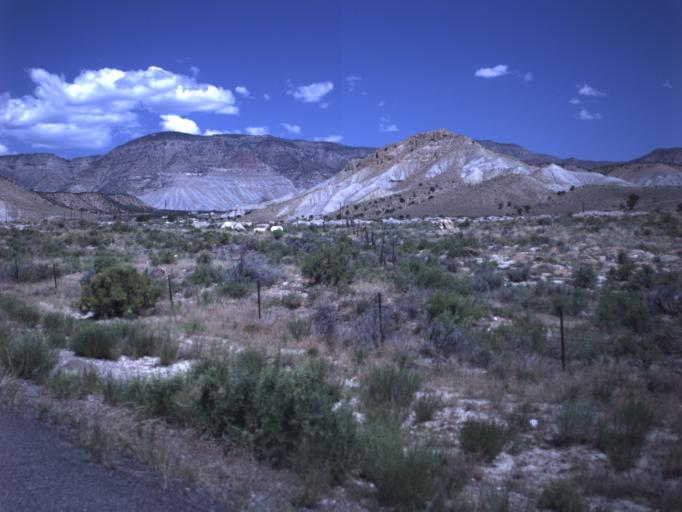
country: US
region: Utah
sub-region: Emery County
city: Orangeville
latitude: 39.2503
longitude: -111.0956
